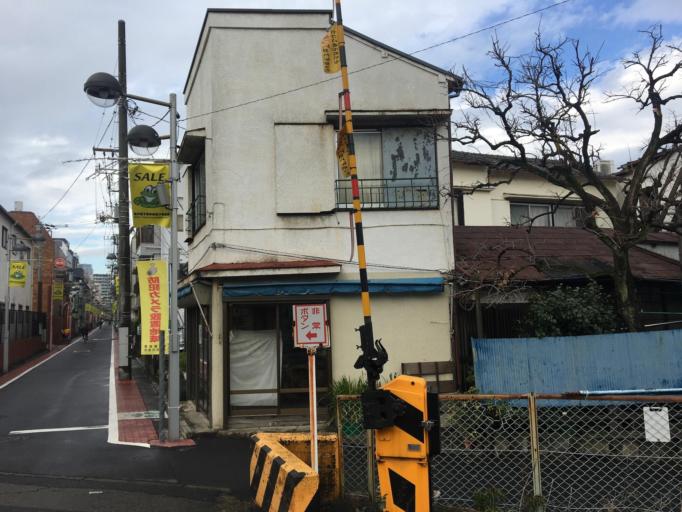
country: JP
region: Tokyo
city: Urayasu
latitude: 35.6984
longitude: 139.8323
